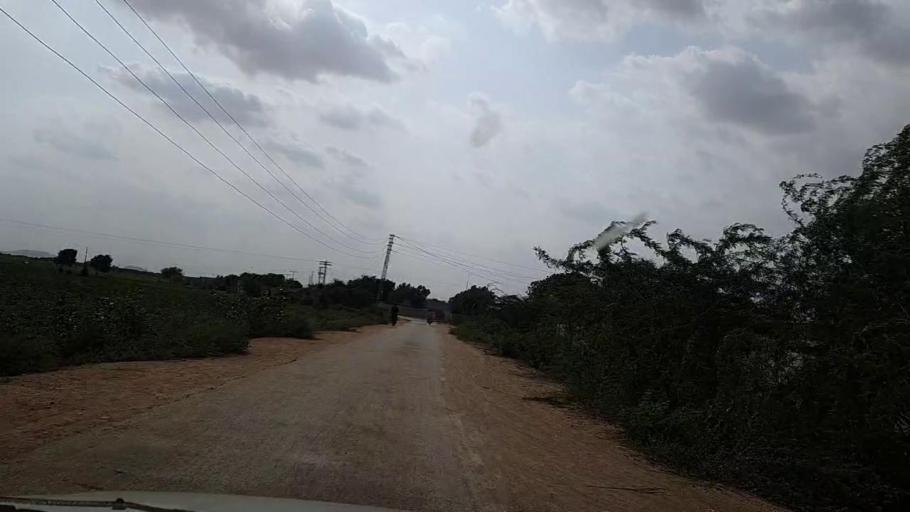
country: PK
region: Sindh
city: Kotri
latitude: 25.2565
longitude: 68.2551
